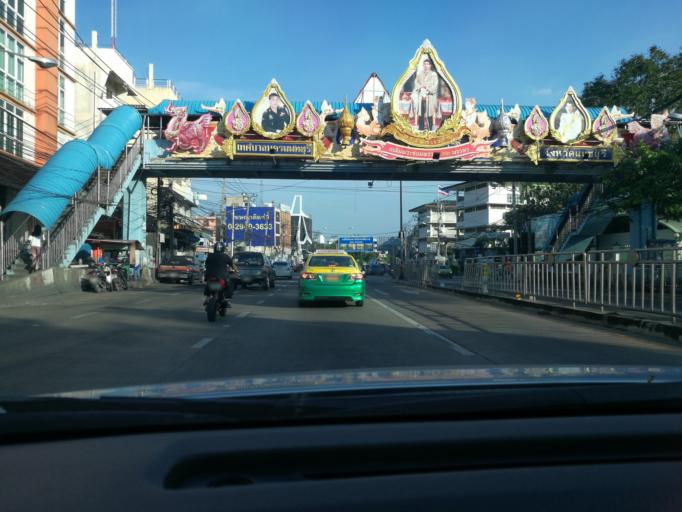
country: TH
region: Bangkok
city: Bang Phlat
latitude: 13.8223
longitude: 100.5055
